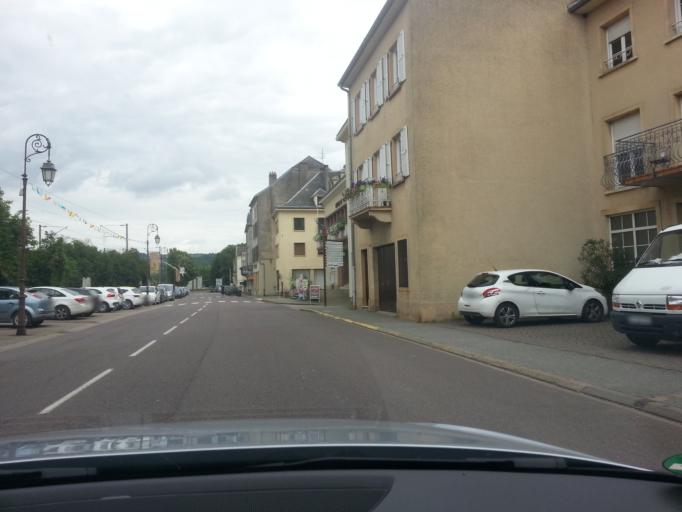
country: FR
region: Lorraine
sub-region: Departement de la Moselle
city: Sierck-les-Bains
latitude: 49.4422
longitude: 6.3591
